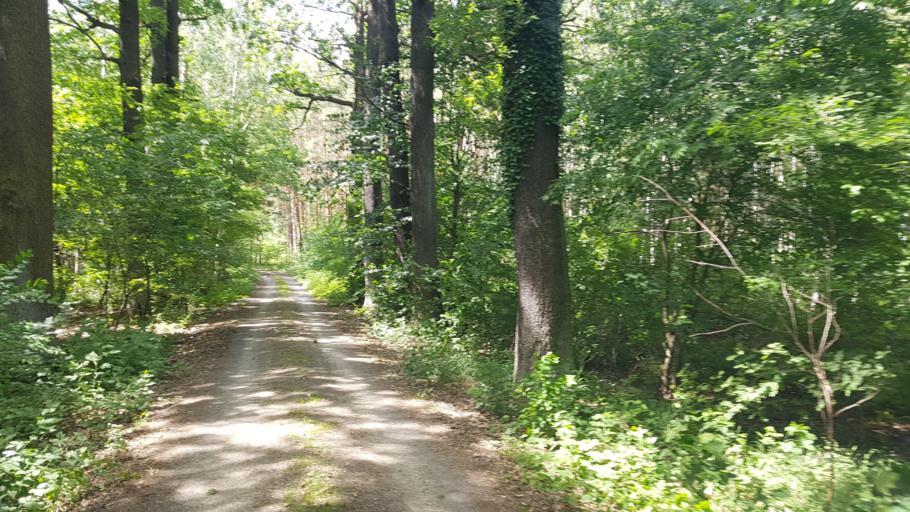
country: DE
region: Brandenburg
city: Plessa
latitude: 51.4890
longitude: 13.6063
